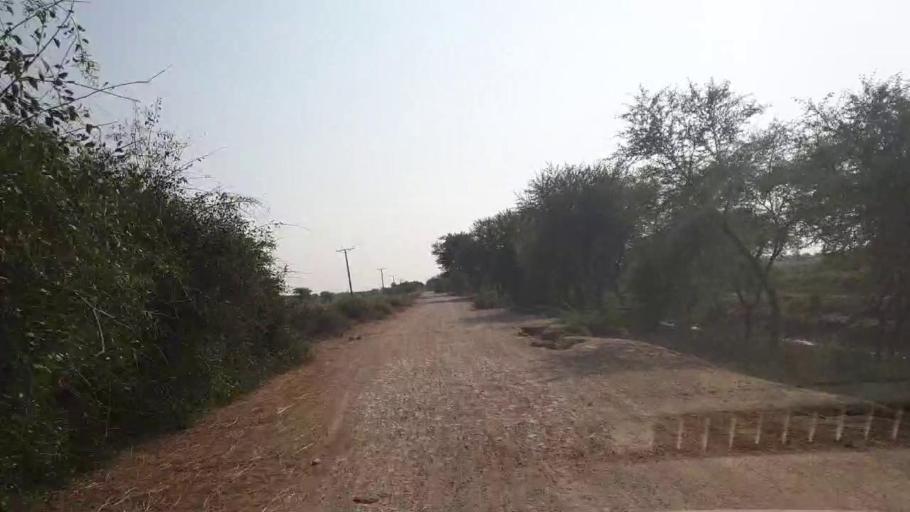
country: PK
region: Sindh
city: Kario
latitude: 24.9005
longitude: 68.6480
